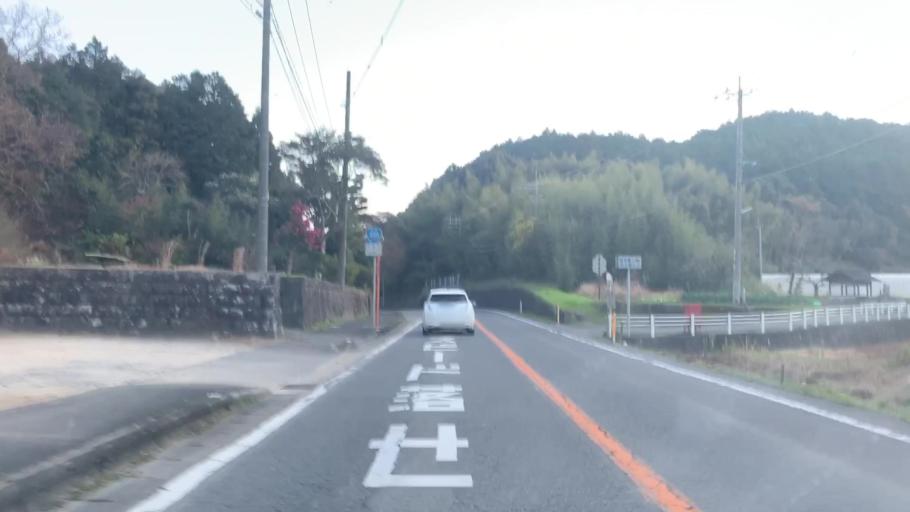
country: JP
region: Saga Prefecture
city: Takeocho-takeo
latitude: 33.2395
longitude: 130.0110
